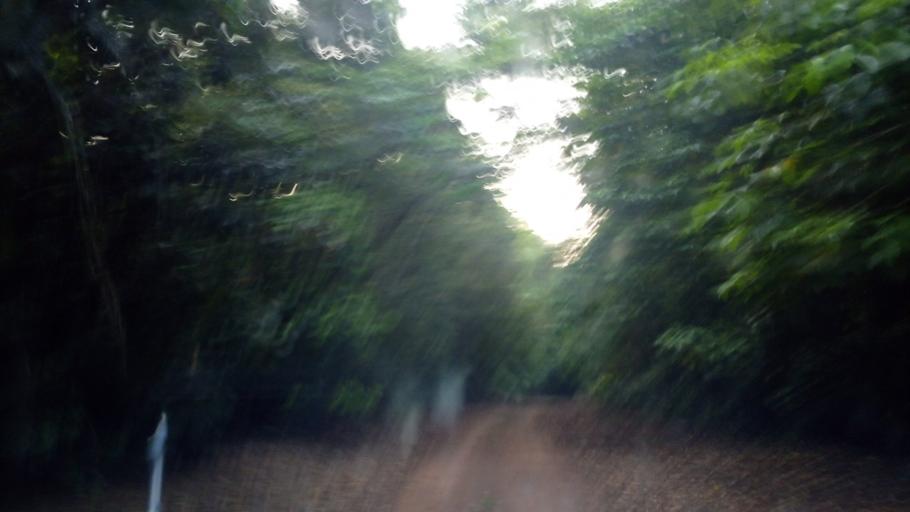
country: AU
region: Queensland
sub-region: Tablelands
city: Atherton
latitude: -17.3774
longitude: 145.7595
